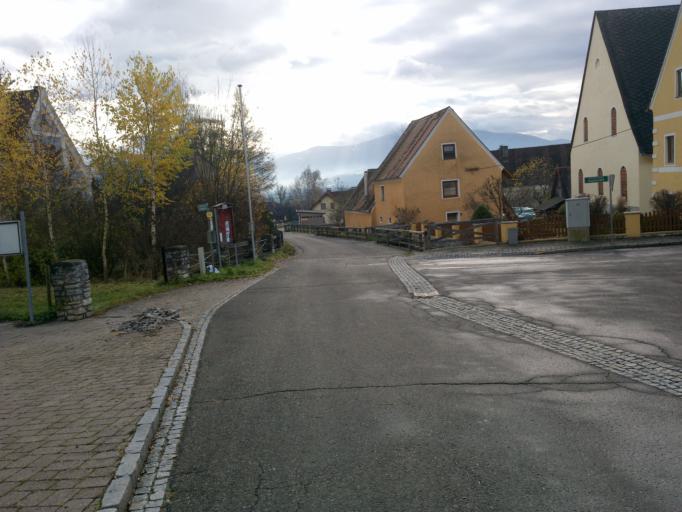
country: AT
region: Styria
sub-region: Politischer Bezirk Murtal
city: Fohnsdorf
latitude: 47.2163
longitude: 14.7012
